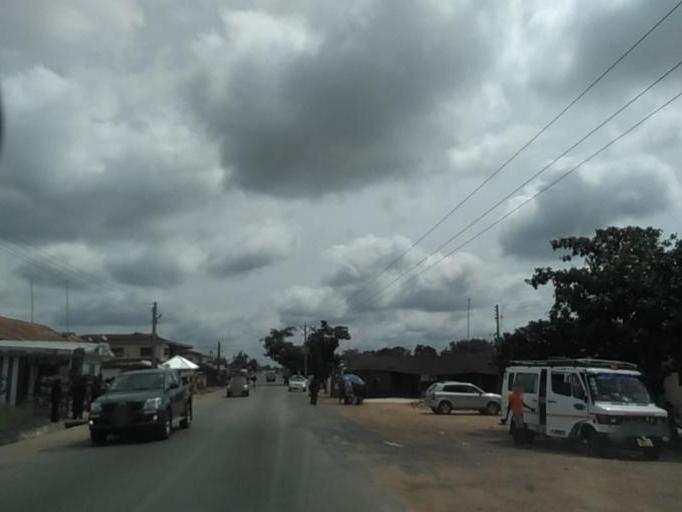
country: GH
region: Ashanti
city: Mamponteng
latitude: 6.7316
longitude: -1.4604
